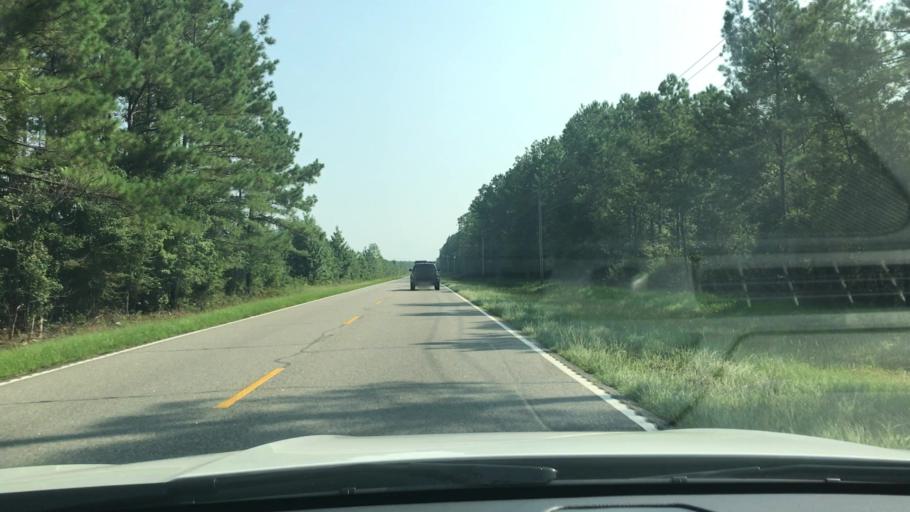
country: US
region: South Carolina
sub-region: Georgetown County
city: Georgetown
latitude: 33.5084
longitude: -79.2534
